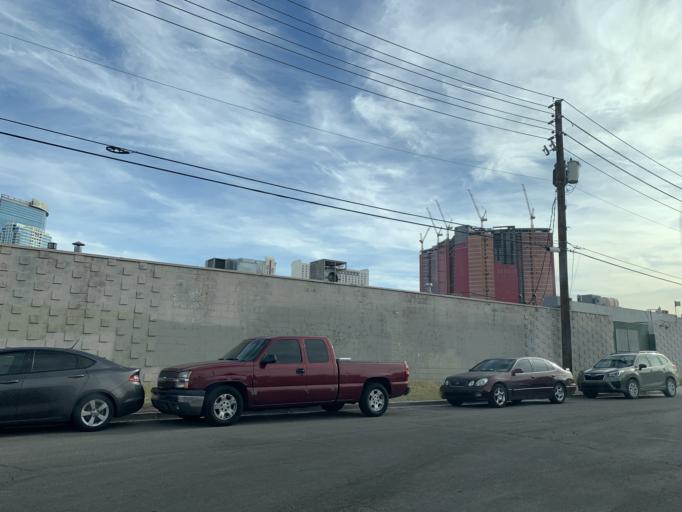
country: US
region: Nevada
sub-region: Clark County
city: Las Vegas
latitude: 36.1422
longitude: -115.1685
